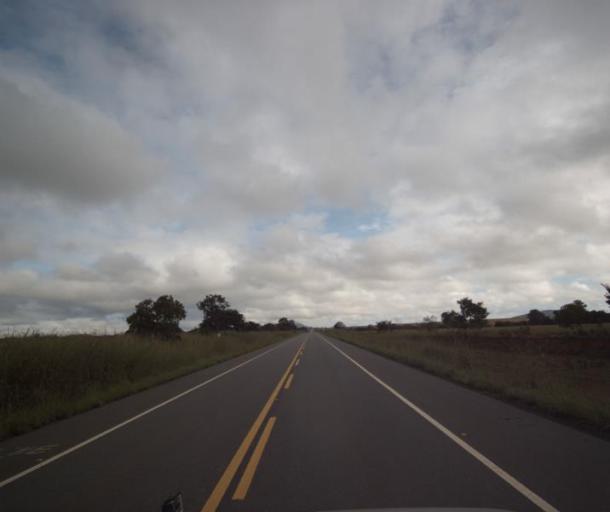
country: BR
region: Goias
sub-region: Padre Bernardo
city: Padre Bernardo
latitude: -15.3079
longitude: -48.6660
